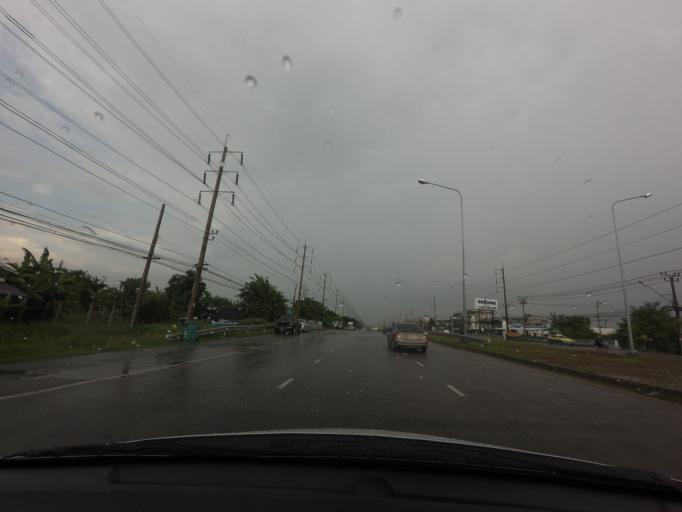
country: TH
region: Bangkok
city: Min Buri
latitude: 13.8148
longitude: 100.7586
